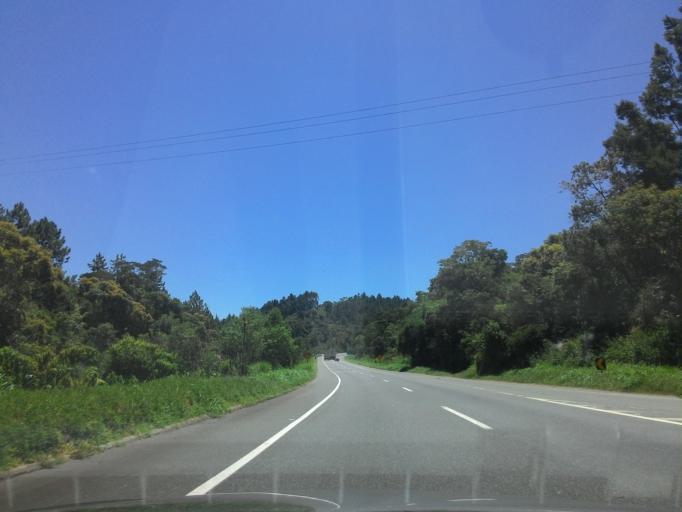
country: BR
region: Sao Paulo
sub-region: Cajati
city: Cajati
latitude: -24.9807
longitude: -48.5043
